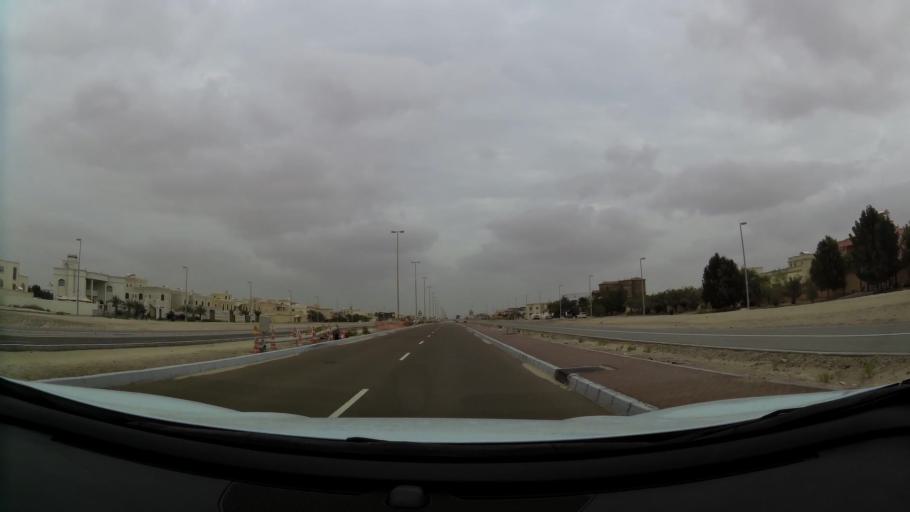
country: AE
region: Abu Dhabi
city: Abu Dhabi
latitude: 24.3743
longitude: 54.6474
